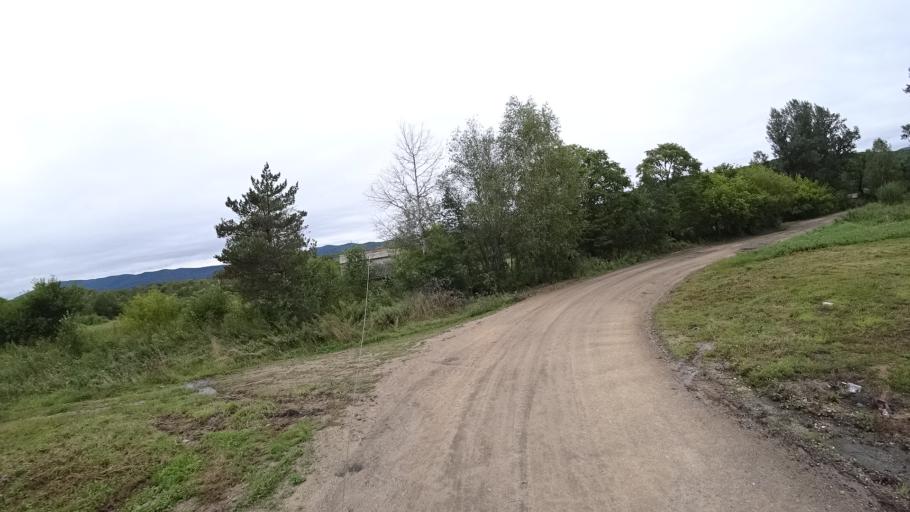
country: RU
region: Primorskiy
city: Rettikhovka
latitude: 44.1630
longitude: 132.7399
